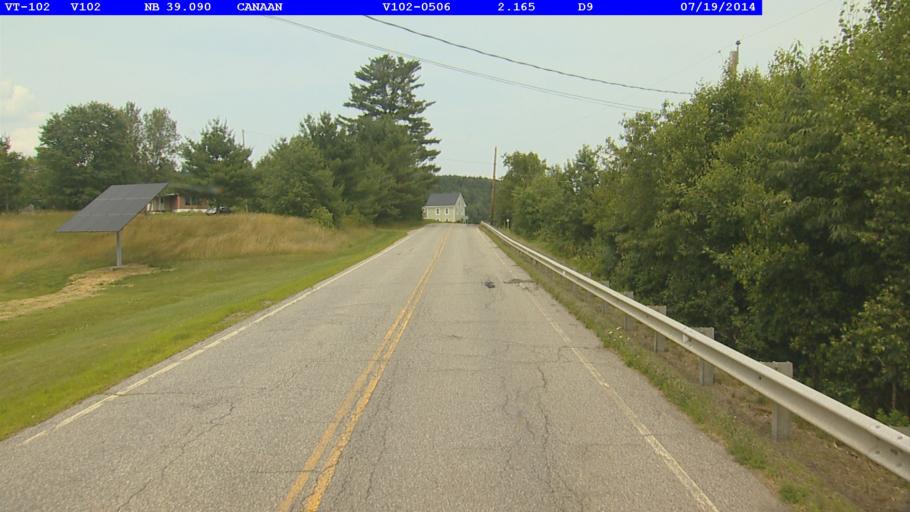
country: US
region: New Hampshire
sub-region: Coos County
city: Colebrook
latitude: 44.9381
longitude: -71.5249
